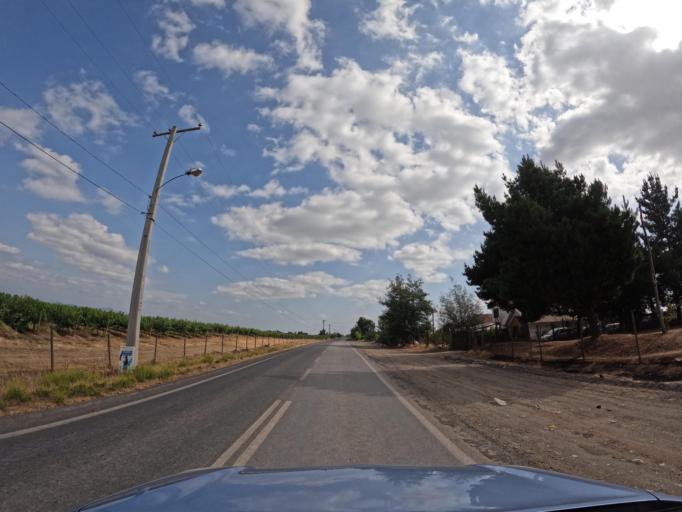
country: CL
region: Maule
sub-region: Provincia de Curico
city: Molina
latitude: -35.1725
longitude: -71.2924
